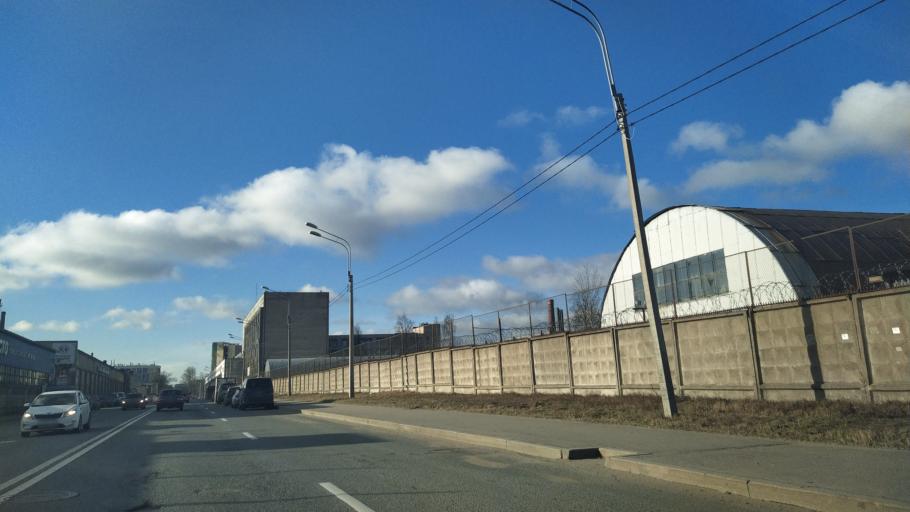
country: RU
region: St.-Petersburg
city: Kushelevka
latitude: 59.9925
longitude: 30.3698
